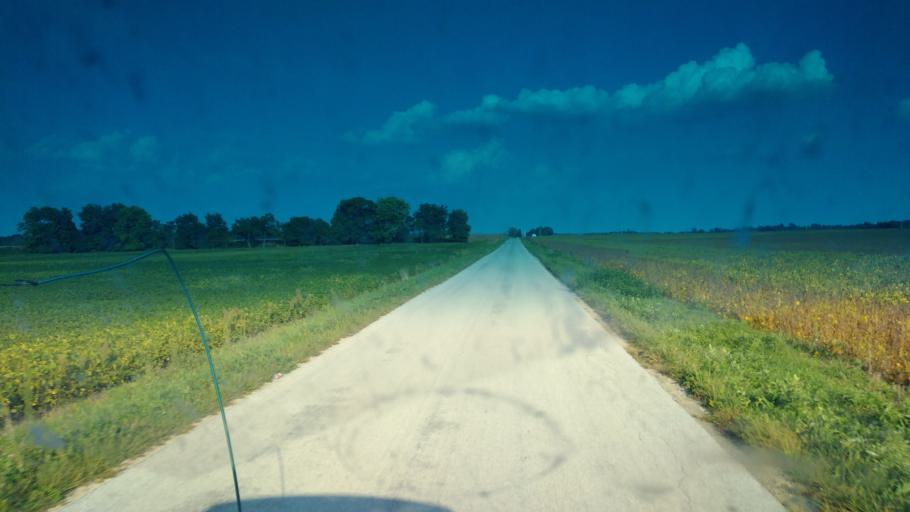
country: US
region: Ohio
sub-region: Wyandot County
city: Upper Sandusky
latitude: 40.9353
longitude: -83.1579
